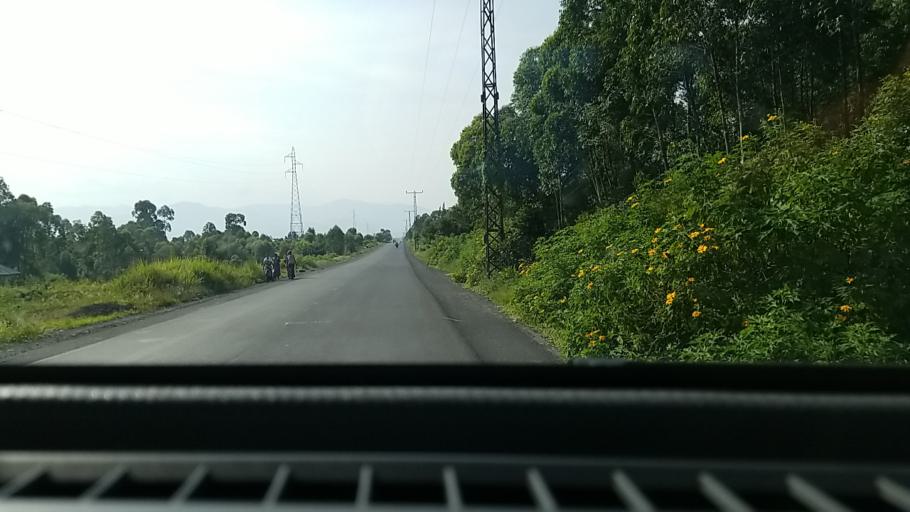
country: CD
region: Nord Kivu
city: Sake
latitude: -1.6050
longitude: 29.1262
